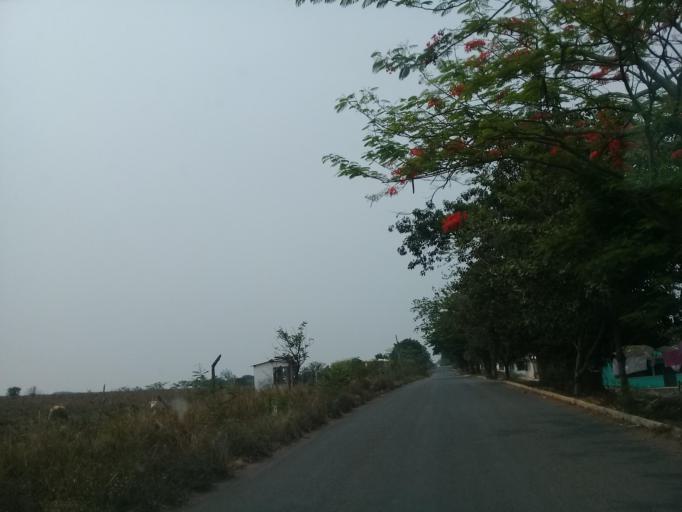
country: MX
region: Veracruz
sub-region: Medellin
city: La Laguna y Monte del Castillo
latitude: 18.9732
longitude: -96.1198
